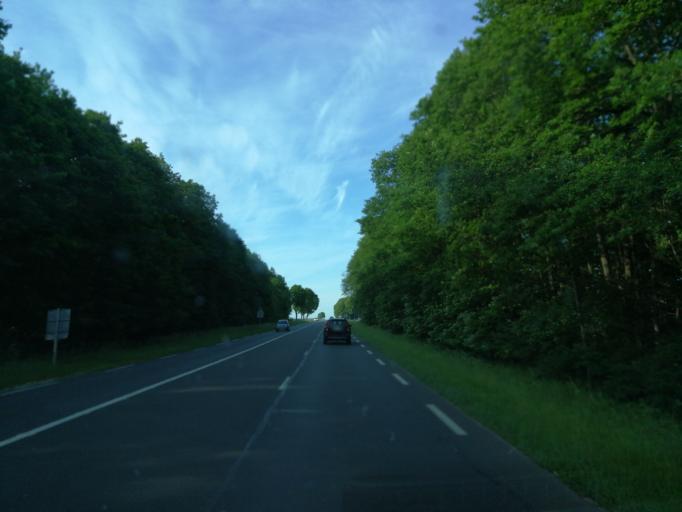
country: FR
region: Centre
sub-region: Departement d'Eure-et-Loir
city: Marboue
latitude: 48.1270
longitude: 1.3354
